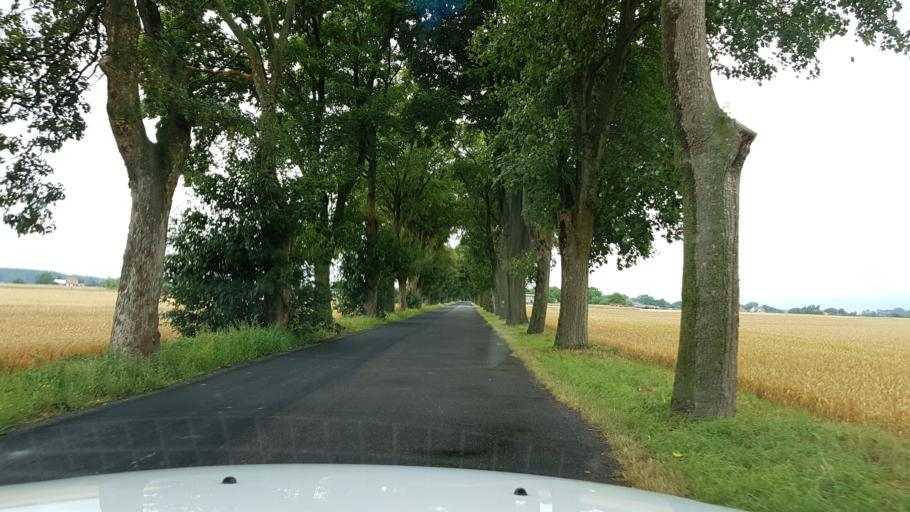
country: PL
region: West Pomeranian Voivodeship
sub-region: Powiat pyrzycki
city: Przelewice
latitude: 53.1063
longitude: 15.1373
